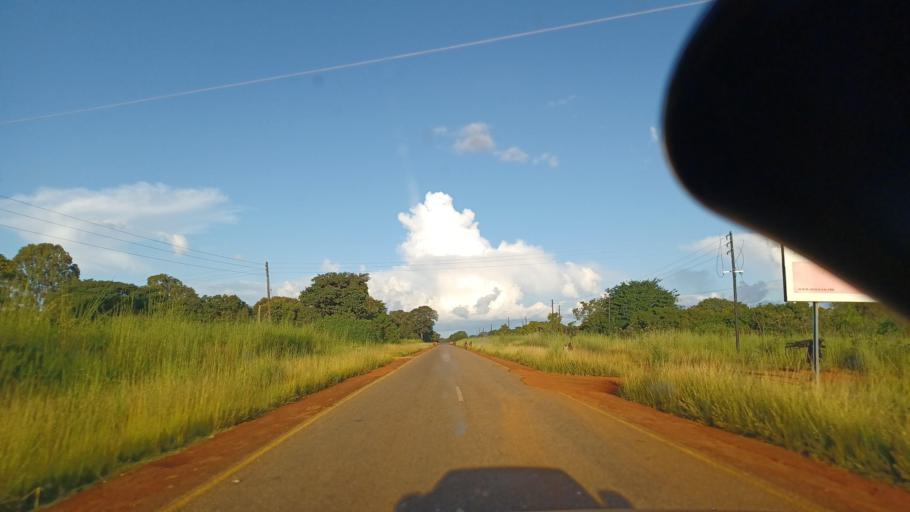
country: ZM
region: North-Western
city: Kalengwa
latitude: -13.1437
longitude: 25.0435
